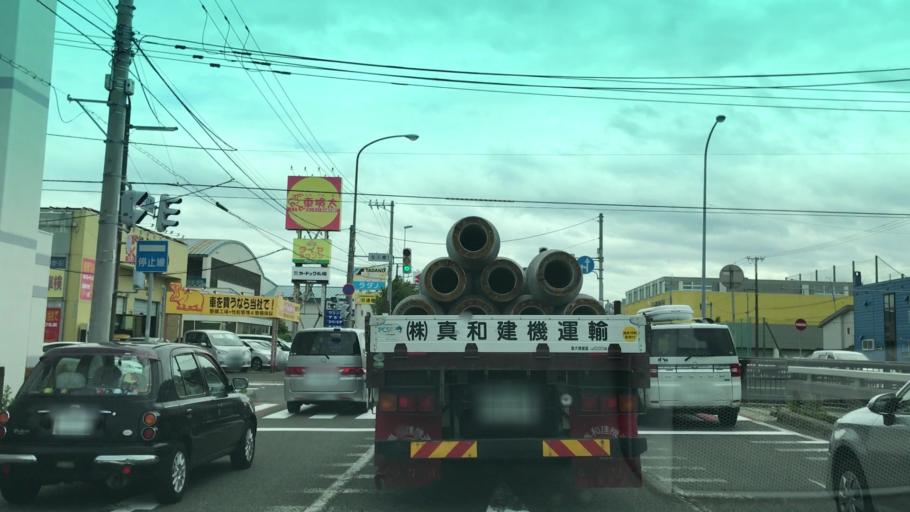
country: JP
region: Hokkaido
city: Sapporo
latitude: 43.0982
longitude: 141.3459
